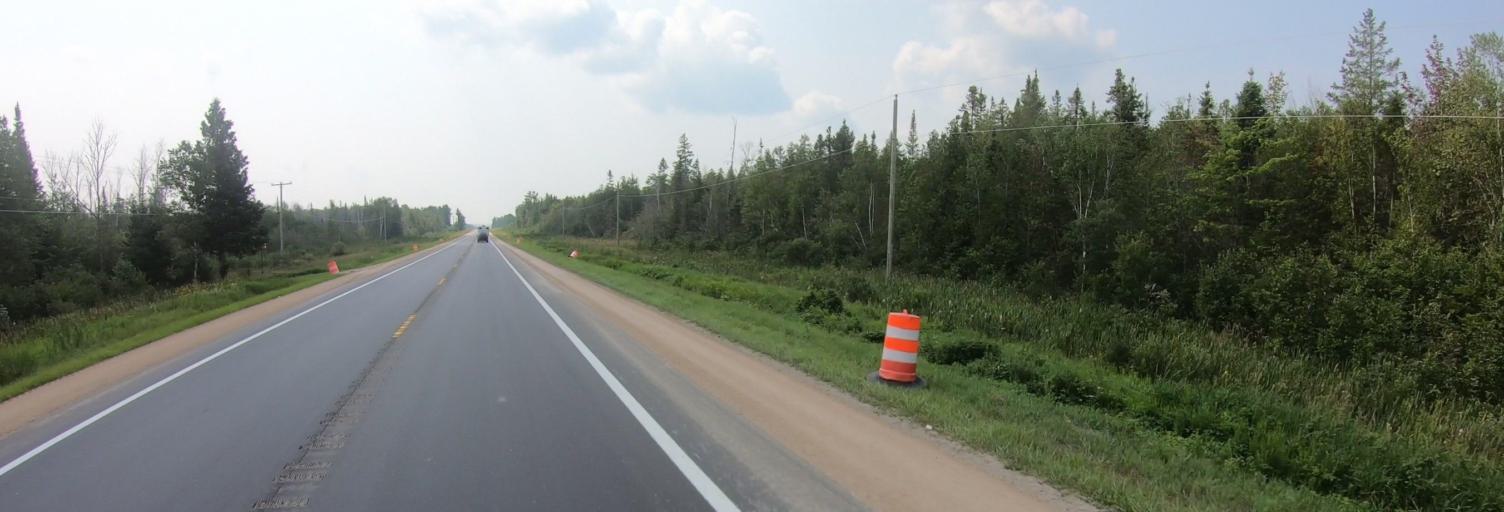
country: US
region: Michigan
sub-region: Luce County
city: Newberry
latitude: 46.4098
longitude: -85.5101
